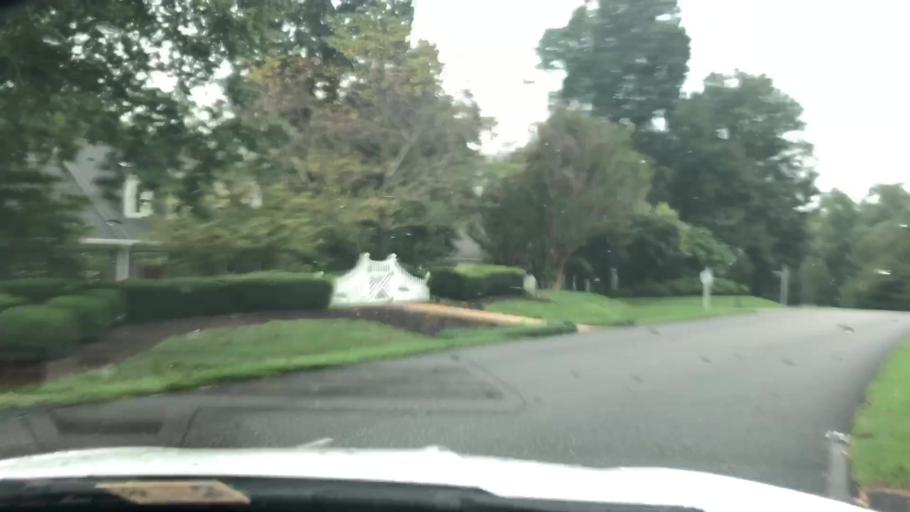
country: US
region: Virginia
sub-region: James City County
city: Williamsburg
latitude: 37.2809
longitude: -76.7711
